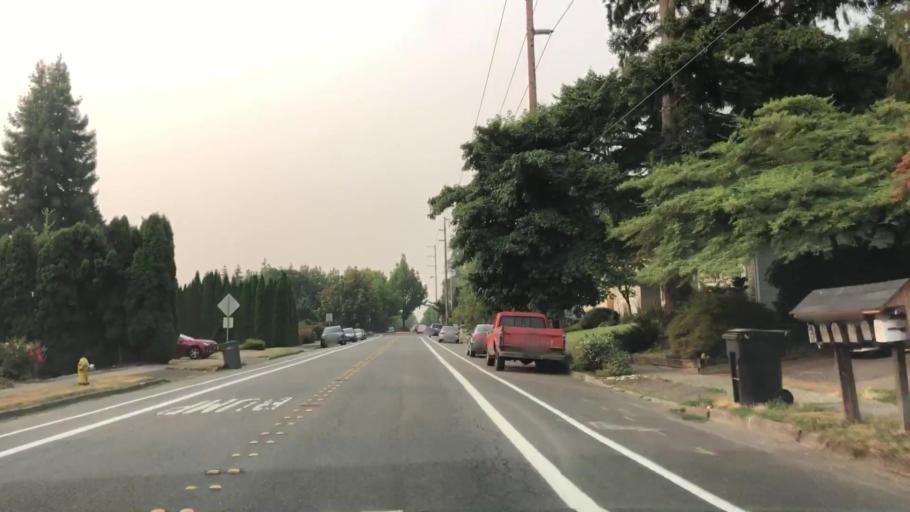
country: US
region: Washington
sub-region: King County
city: Redmond
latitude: 47.6559
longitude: -122.1325
